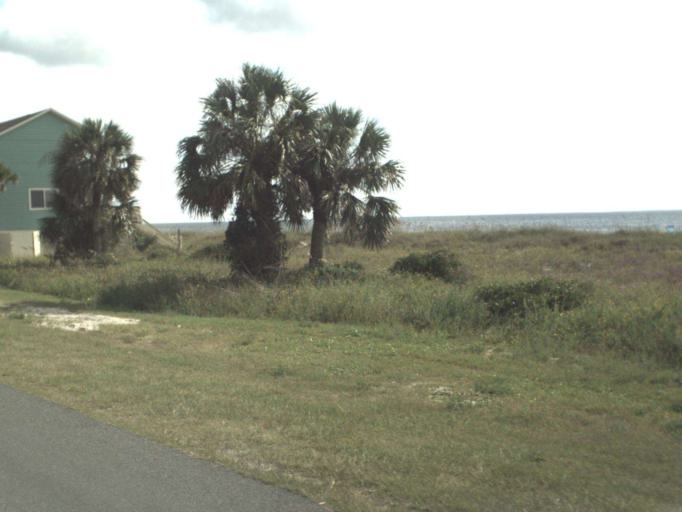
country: US
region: Florida
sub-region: Bay County
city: Mexico Beach
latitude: 29.8992
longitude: -85.3634
